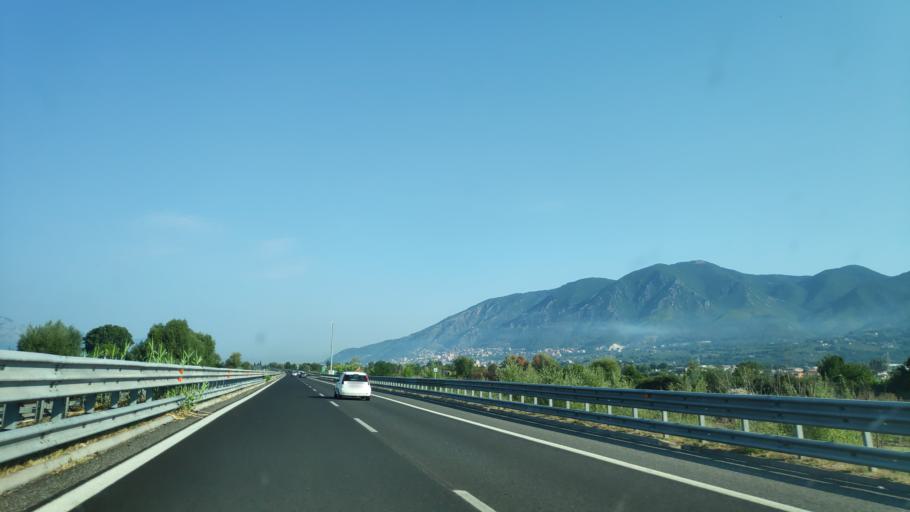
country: IT
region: Campania
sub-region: Provincia di Salerno
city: Sala Consilina
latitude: 40.3567
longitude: 15.6126
